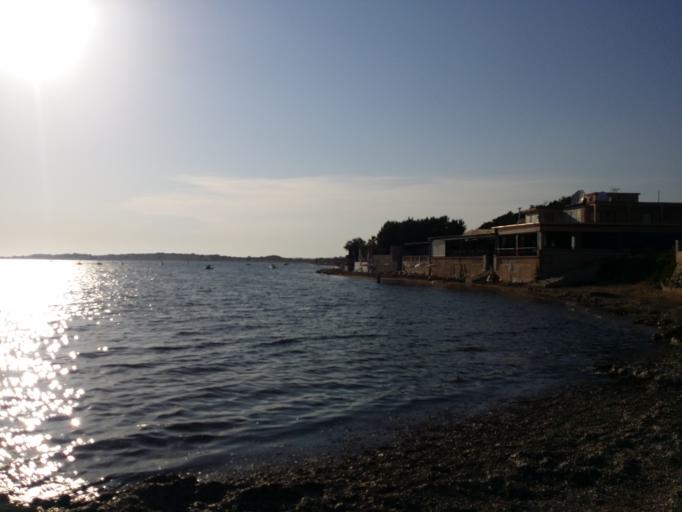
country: GR
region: Ionian Islands
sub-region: Nomos Kerkyras
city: Perivoli
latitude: 39.4265
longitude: 19.9435
